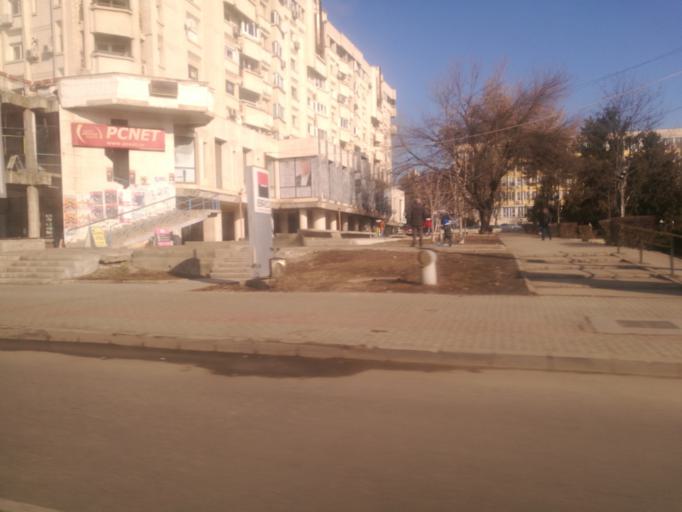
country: RO
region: Iasi
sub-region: Municipiul Iasi
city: Iasi
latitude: 47.1683
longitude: 27.5801
